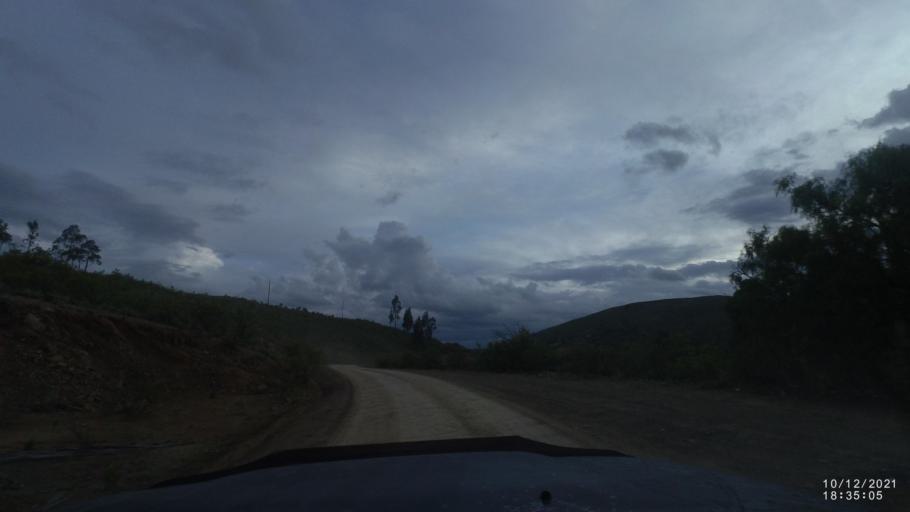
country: BO
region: Cochabamba
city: Tarata
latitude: -17.8256
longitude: -65.9905
